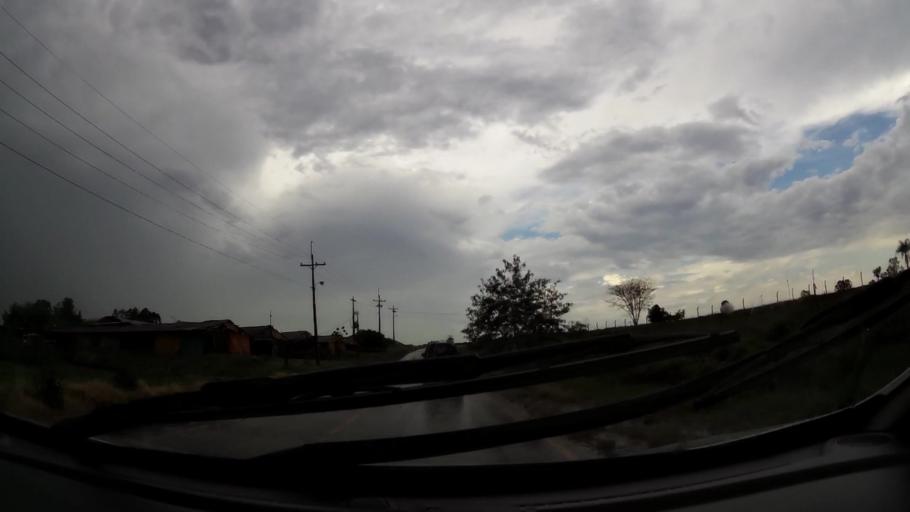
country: PY
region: Alto Parana
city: Presidente Franco
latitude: -25.5825
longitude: -54.6710
